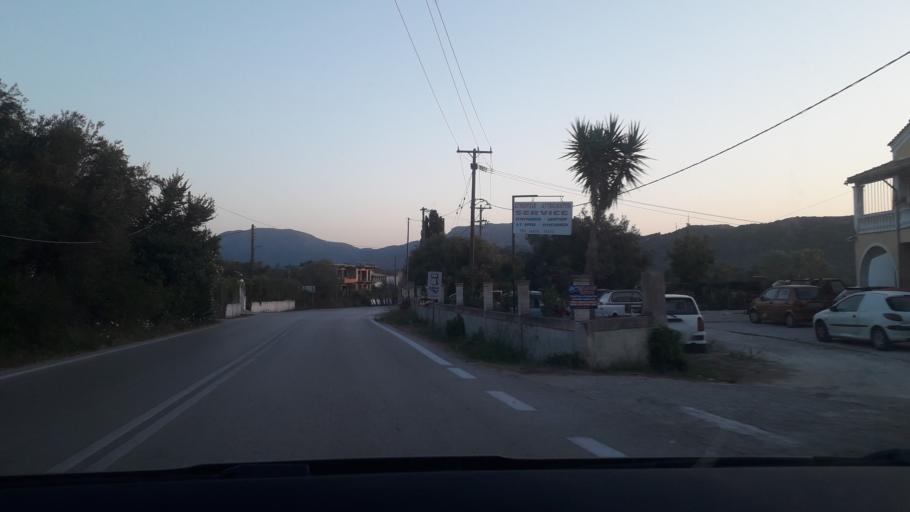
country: GR
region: Ionian Islands
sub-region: Nomos Kerkyras
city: Agios Matthaios
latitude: 39.4706
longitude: 19.9113
